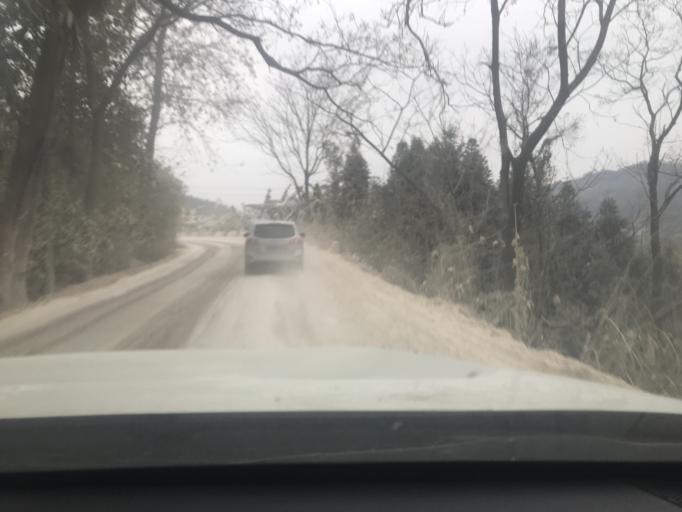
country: CN
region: Guangxi Zhuangzu Zizhiqu
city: Xinzhou
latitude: 25.0066
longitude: 105.8406
